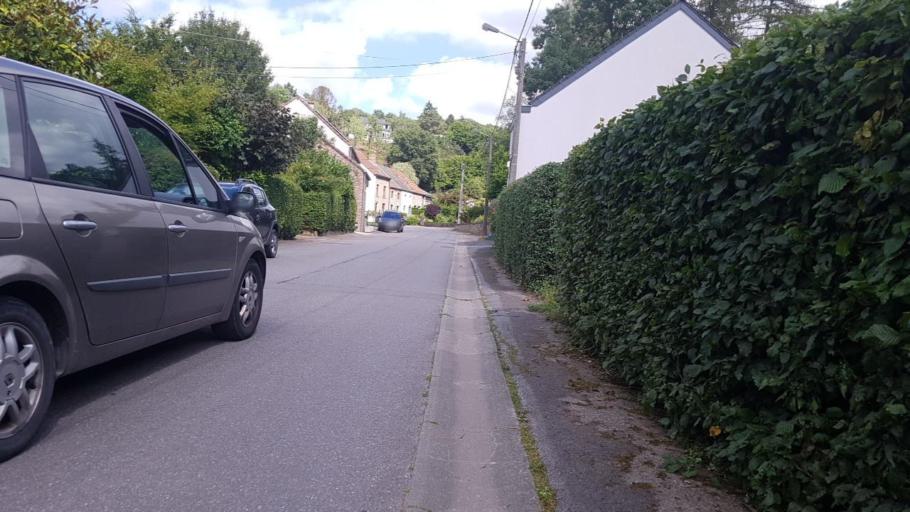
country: BE
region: Wallonia
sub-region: Province du Hainaut
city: Charleroi
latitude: 50.3530
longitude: 4.4151
